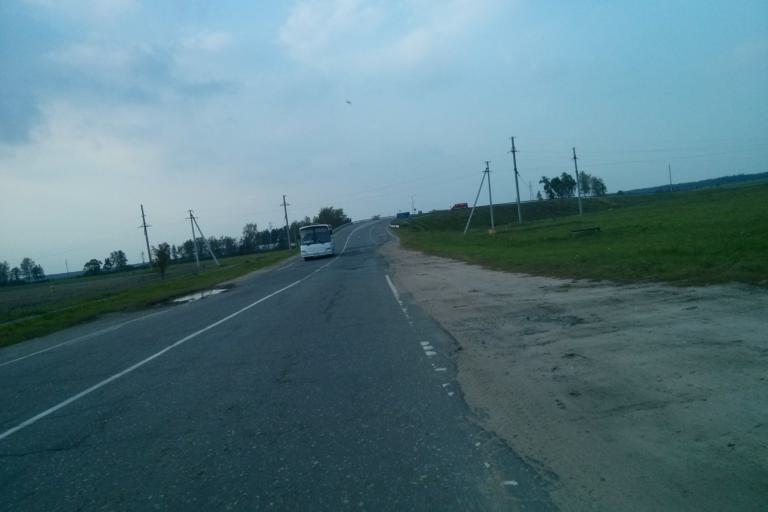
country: BY
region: Minsk
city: Chervyen'
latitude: 53.7201
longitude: 28.3967
